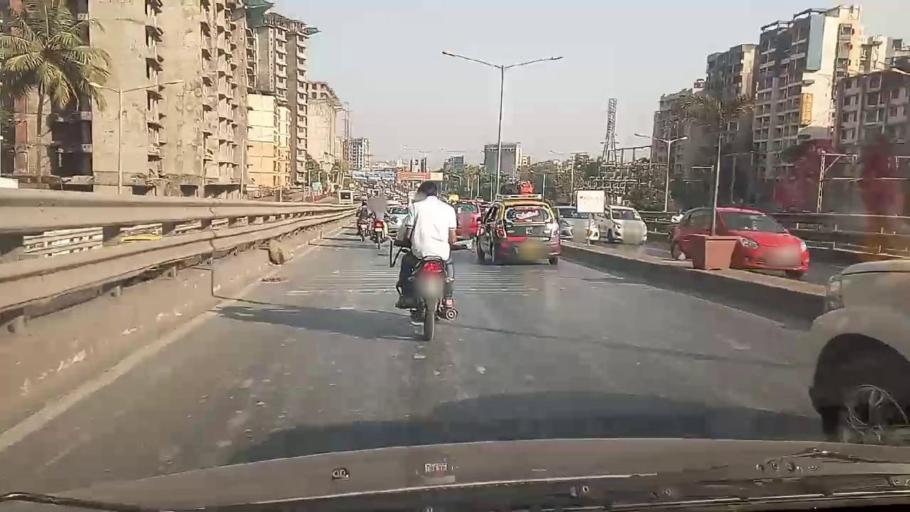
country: IN
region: Maharashtra
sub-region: Mumbai Suburban
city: Mumbai
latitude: 19.0656
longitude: 72.8922
